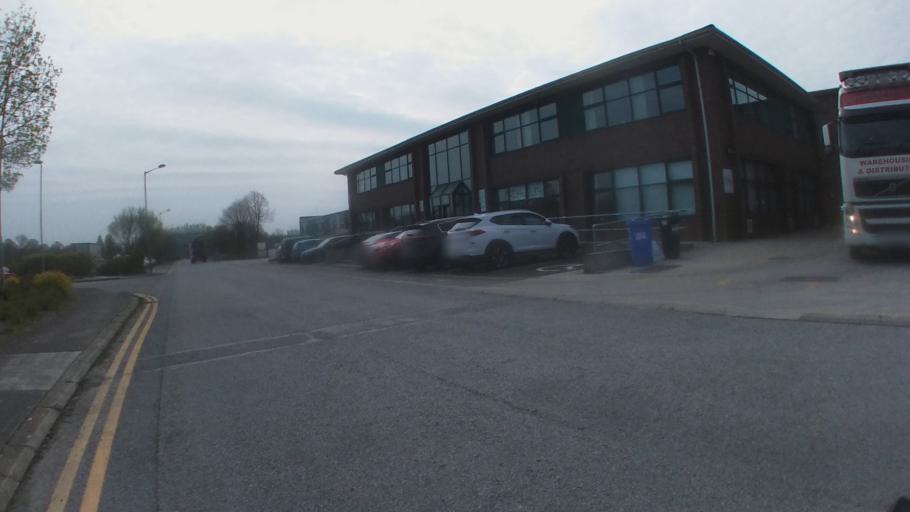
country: IE
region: Leinster
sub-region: Kilkenny
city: Kilkenny
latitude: 52.6457
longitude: -7.2116
